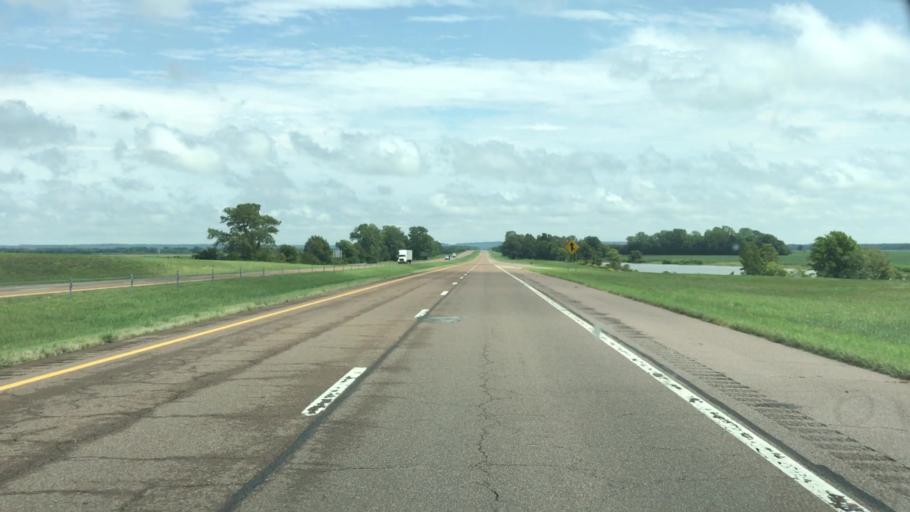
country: US
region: Missouri
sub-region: Pemiscot County
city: Caruthersville
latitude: 36.0927
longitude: -89.5845
